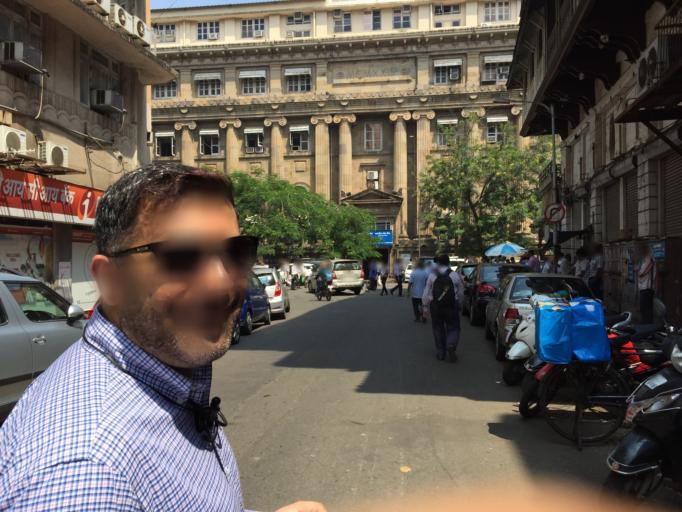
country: IN
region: Maharashtra
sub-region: Raigarh
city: Uran
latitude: 18.9311
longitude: 72.8337
